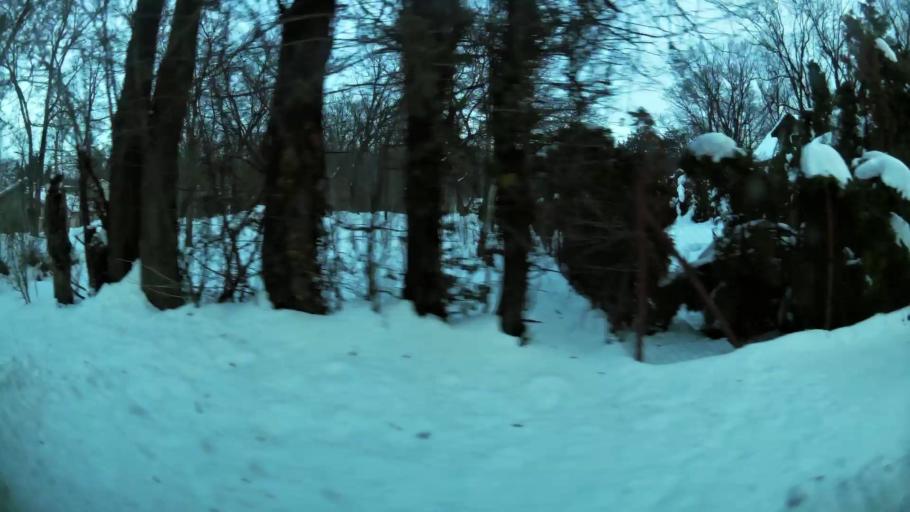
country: RS
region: Central Serbia
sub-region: Belgrade
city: Palilula
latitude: 44.8015
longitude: 20.5023
